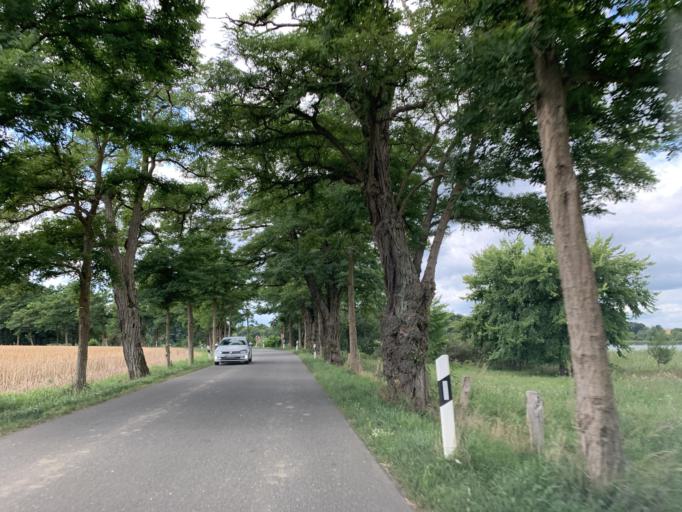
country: DE
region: Mecklenburg-Vorpommern
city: Blankensee
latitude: 53.4015
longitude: 13.2302
